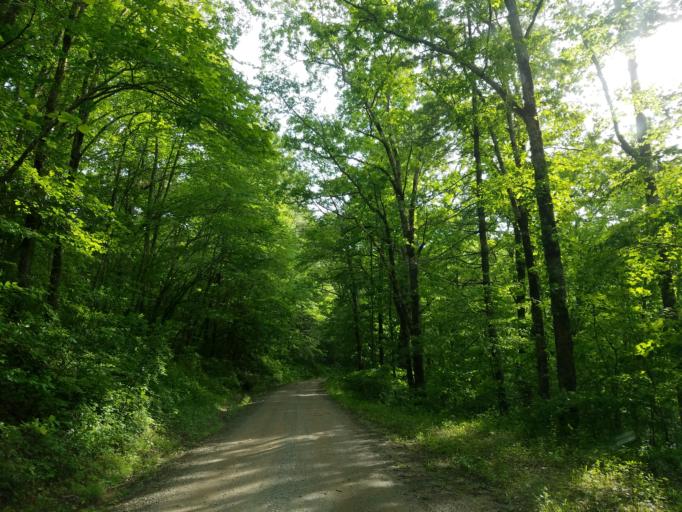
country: US
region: Georgia
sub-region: Union County
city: Blairsville
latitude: 34.7525
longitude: -84.0135
